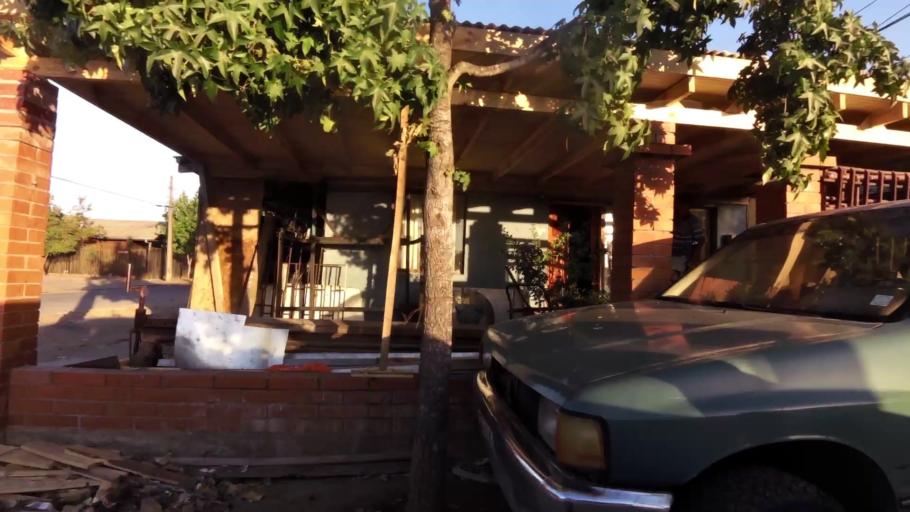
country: CL
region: Maule
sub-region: Provincia de Talca
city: Talca
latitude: -35.4413
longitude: -71.6384
